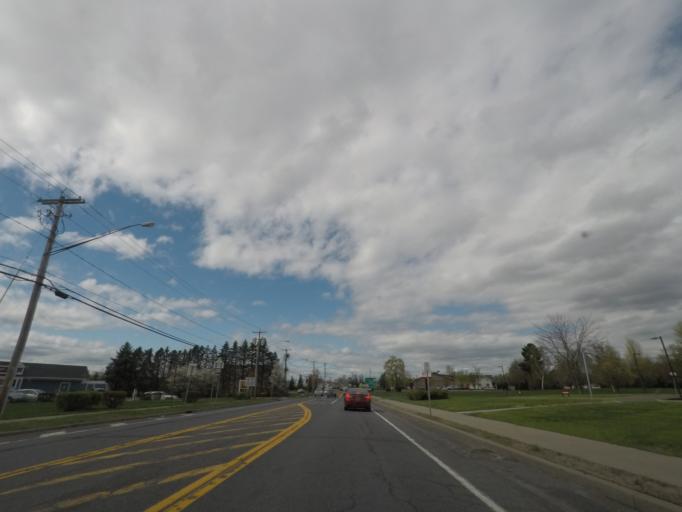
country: US
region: New York
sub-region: Columbia County
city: Valatie
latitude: 42.4264
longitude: -73.6877
